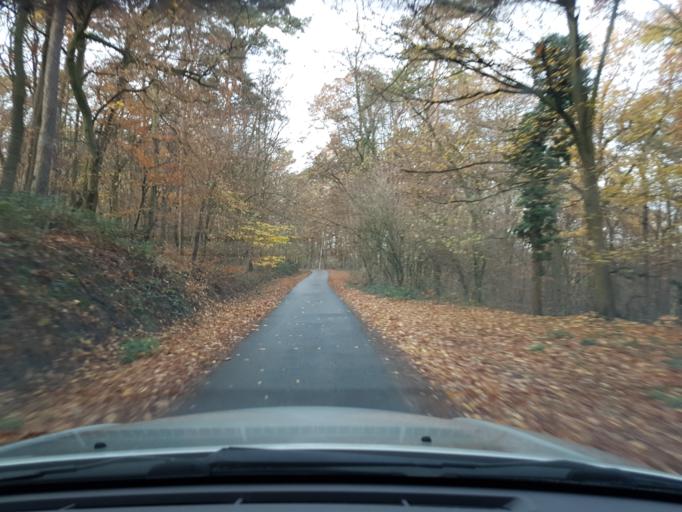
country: DE
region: Hesse
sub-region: Regierungsbezirk Darmstadt
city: Kiedrich
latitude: 50.0383
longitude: 8.0503
